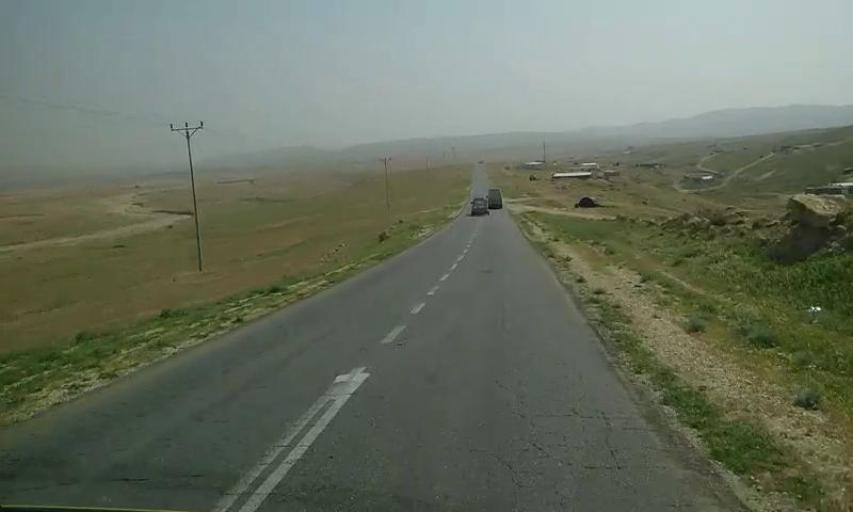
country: PS
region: West Bank
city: An Nuway`imah
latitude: 31.9199
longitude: 35.3967
